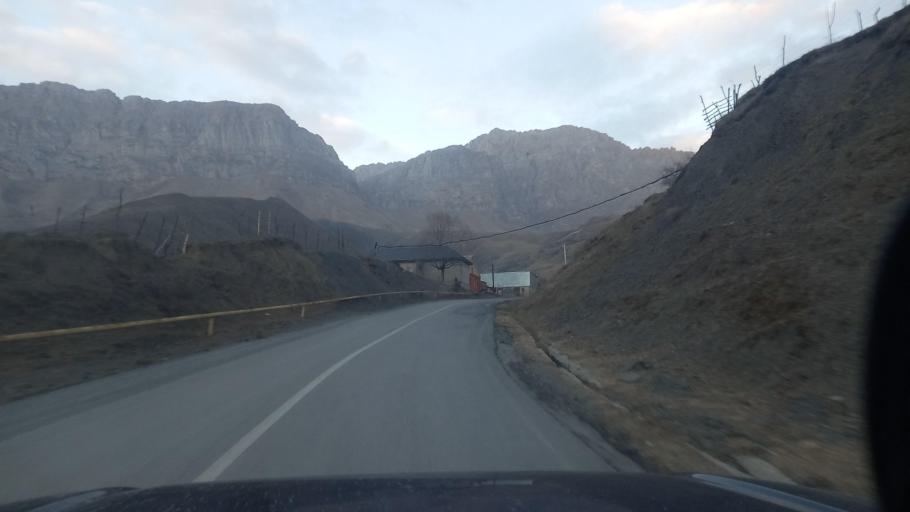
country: RU
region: Ingushetiya
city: Dzhayrakh
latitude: 42.8104
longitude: 44.7989
